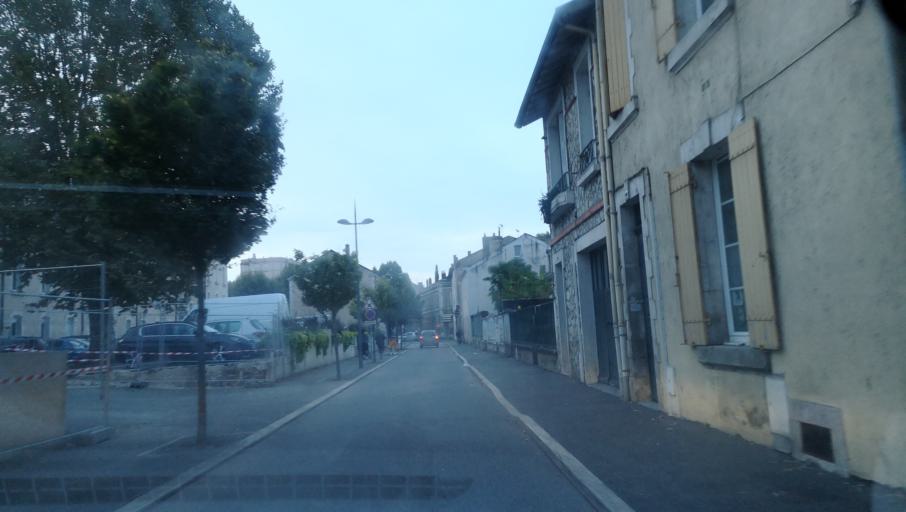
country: FR
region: Midi-Pyrenees
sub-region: Departement du Lot
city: Cahors
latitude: 44.4523
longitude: 1.4377
